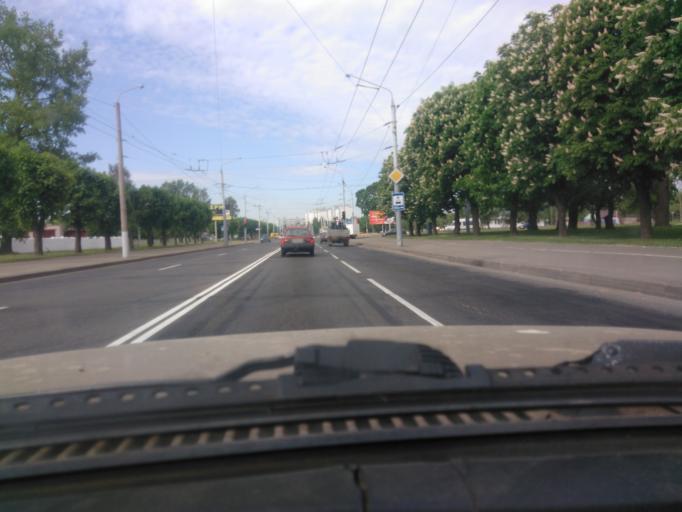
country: BY
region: Mogilev
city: Buynichy
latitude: 53.8893
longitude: 30.2855
